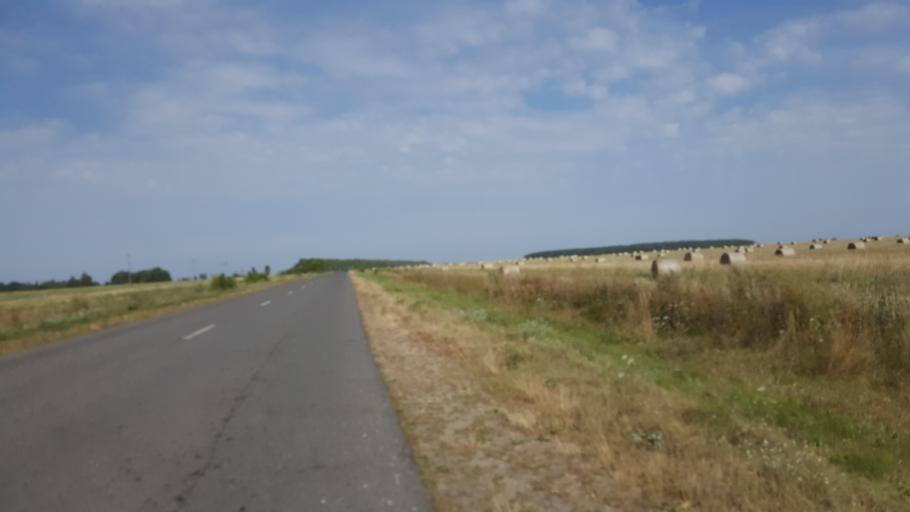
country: BY
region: Brest
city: Kamyanyets
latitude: 52.4369
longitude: 23.7462
